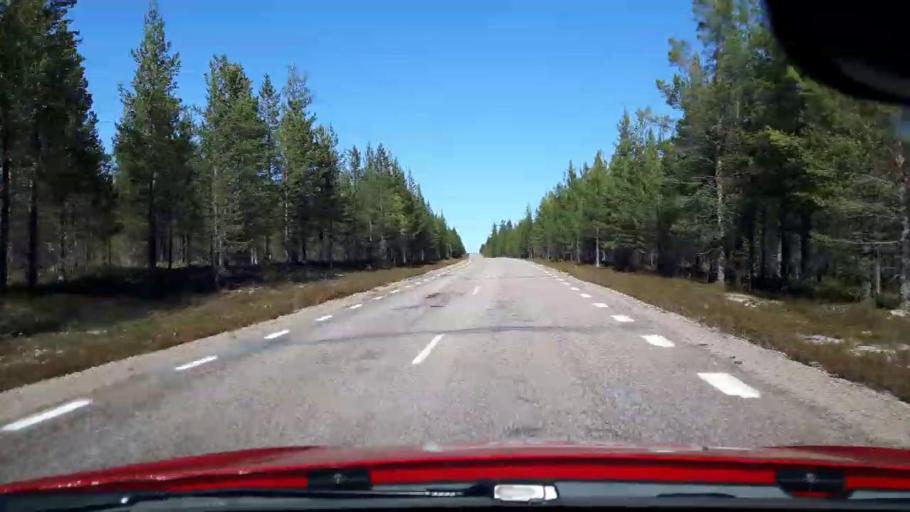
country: SE
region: Jaemtland
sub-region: Harjedalens Kommun
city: Sveg
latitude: 61.7195
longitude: 14.1681
